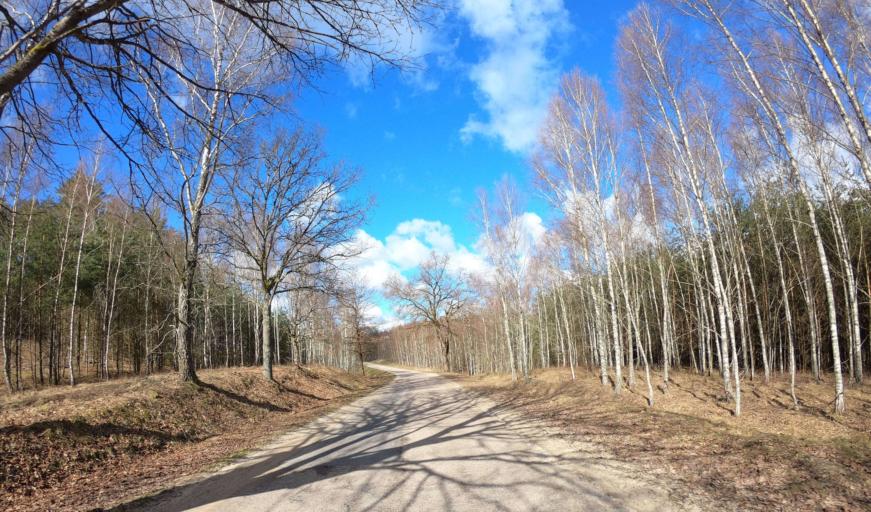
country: PL
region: West Pomeranian Voivodeship
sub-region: Powiat drawski
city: Zlocieniec
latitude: 53.4803
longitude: 15.9220
